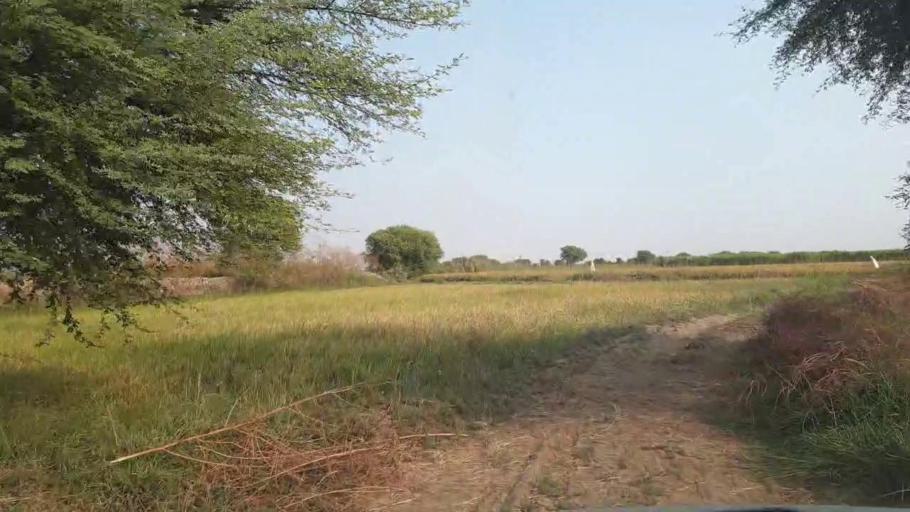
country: PK
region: Sindh
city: Matli
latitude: 25.0478
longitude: 68.7490
